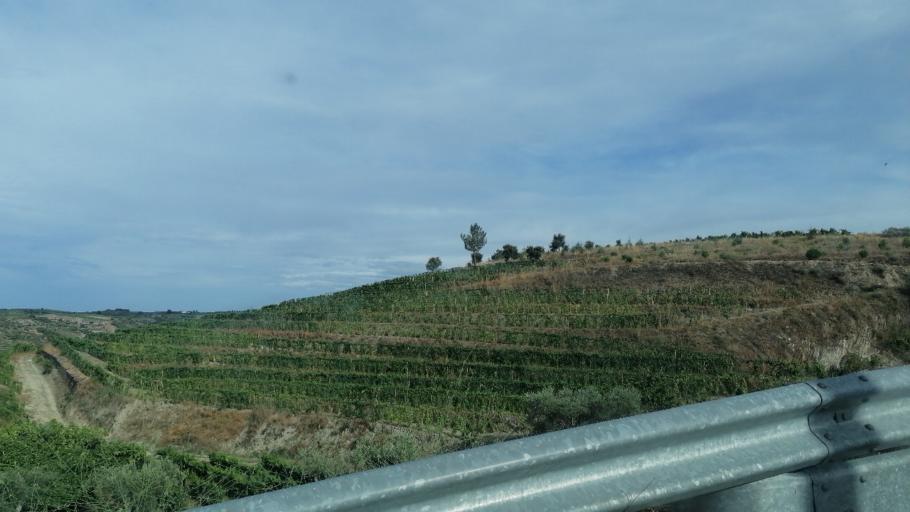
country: PT
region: Viseu
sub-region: Sao Joao da Pesqueira
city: Sao Joao da Pesqueira
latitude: 41.0948
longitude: -7.4678
